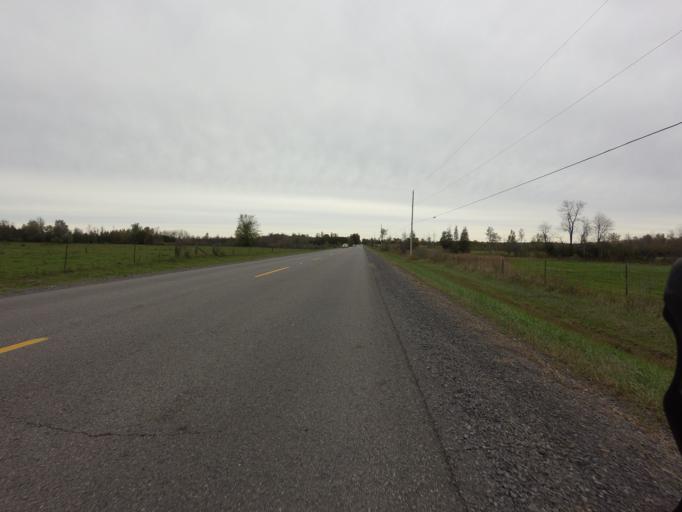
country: CA
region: Ontario
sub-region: Lanark County
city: Smiths Falls
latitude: 44.8486
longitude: -75.8141
